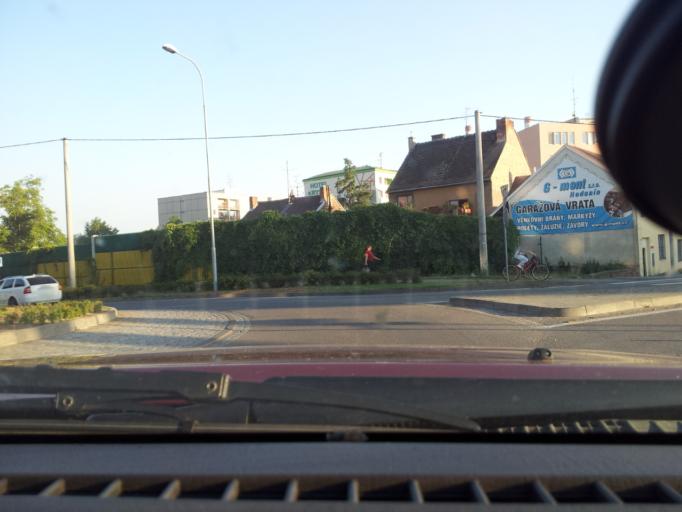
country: CZ
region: South Moravian
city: Hodonin
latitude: 48.8515
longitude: 17.1219
